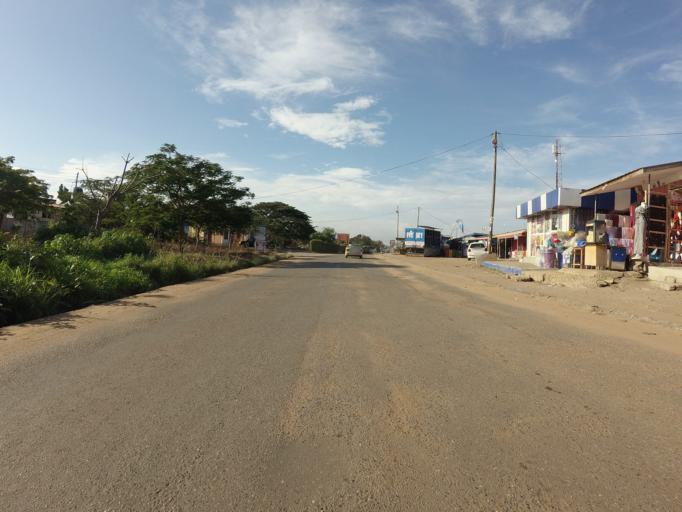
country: GH
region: Greater Accra
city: Nungua
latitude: 5.6505
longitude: -0.0643
